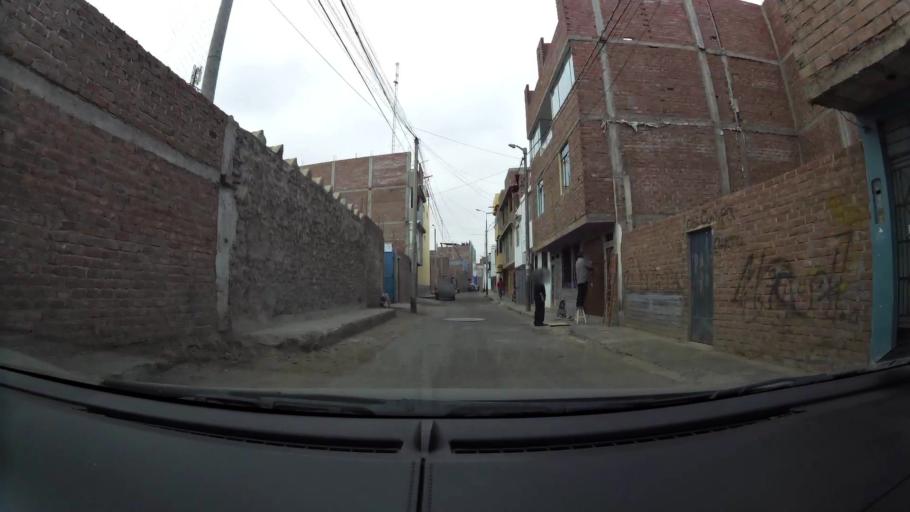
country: PE
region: La Libertad
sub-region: Provincia de Trujillo
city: Trujillo
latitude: -8.1002
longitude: -79.0251
